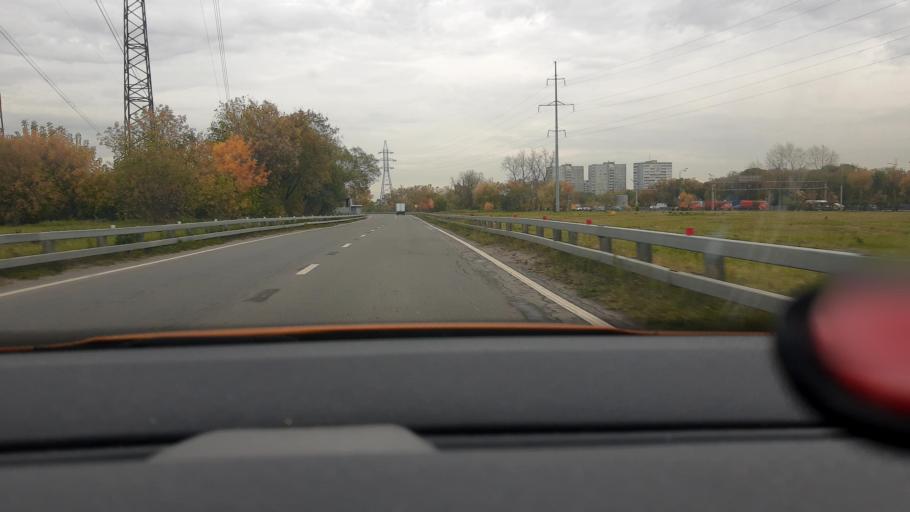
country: RU
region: Moscow
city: Zhulebino
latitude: 55.7093
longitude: 37.8579
